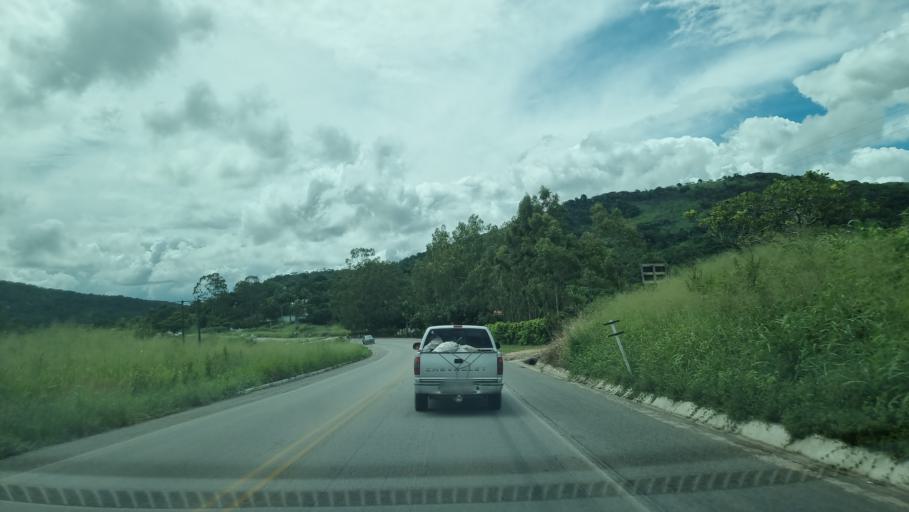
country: BR
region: Pernambuco
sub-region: Caruaru
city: Caruaru
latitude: -8.3732
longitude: -35.9838
